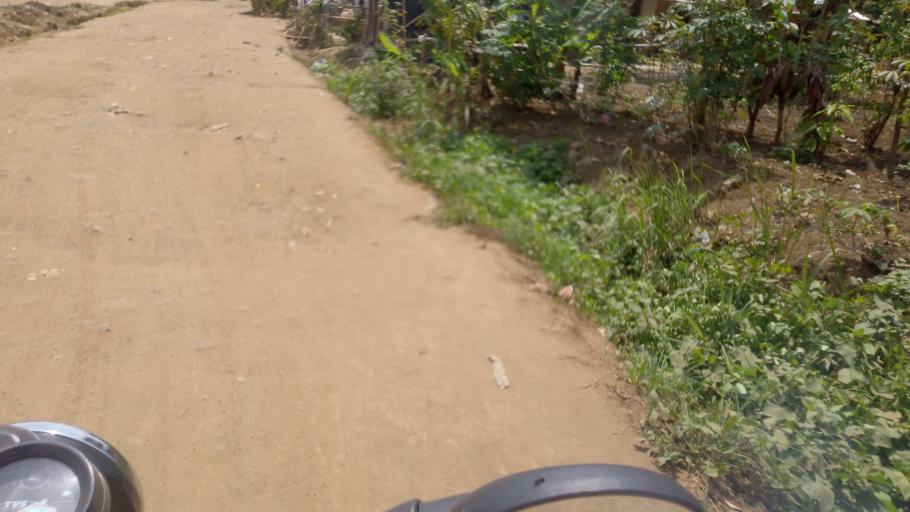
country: SL
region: Western Area
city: Waterloo
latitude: 8.3245
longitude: -13.0751
